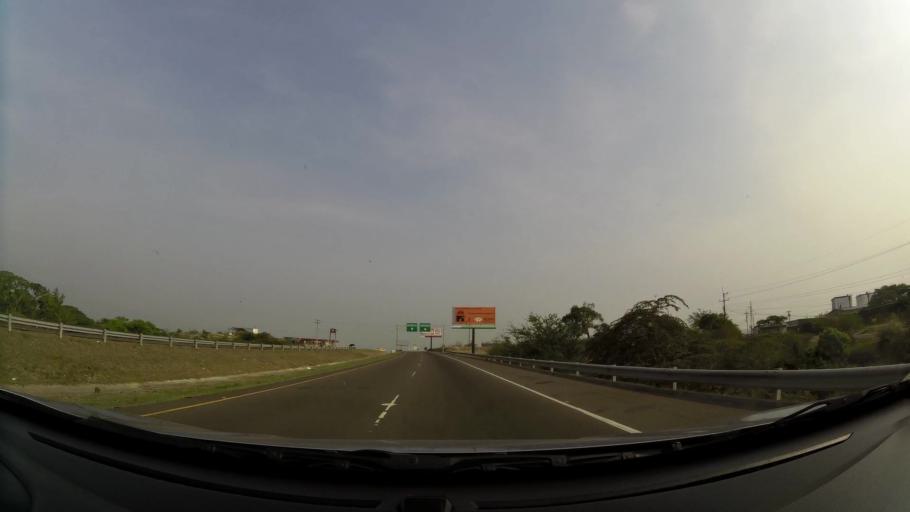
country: HN
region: Comayagua
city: Comayagua
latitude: 14.4202
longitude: -87.6272
